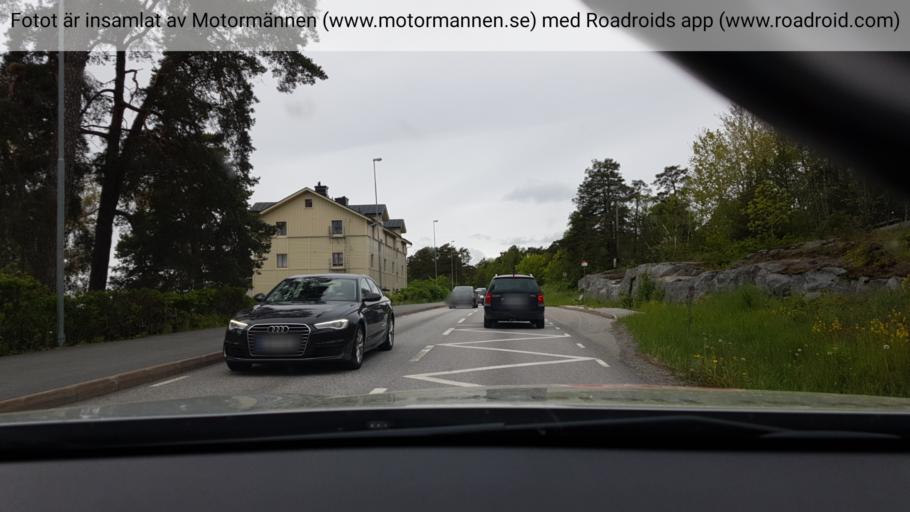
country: SE
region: Stockholm
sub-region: Vaxholms Kommun
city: Vaxholm
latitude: 59.4027
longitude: 18.3721
